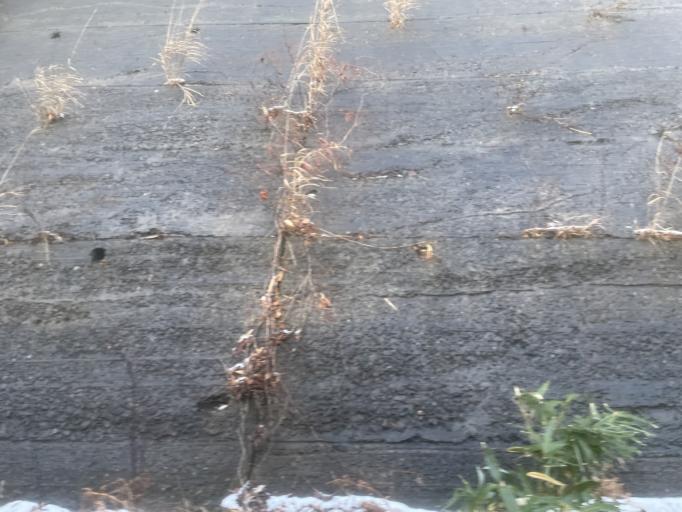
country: JP
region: Aomori
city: Goshogawara
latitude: 41.0771
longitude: 140.5391
